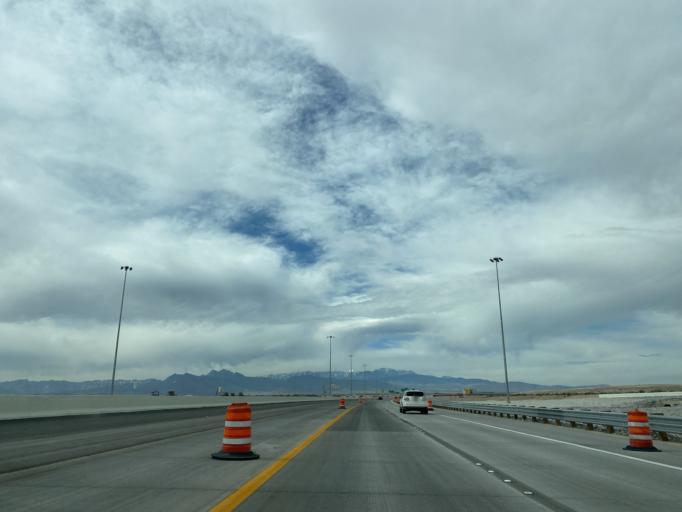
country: US
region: Nevada
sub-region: Clark County
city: Nellis Air Force Base
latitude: 36.2898
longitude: -115.1186
